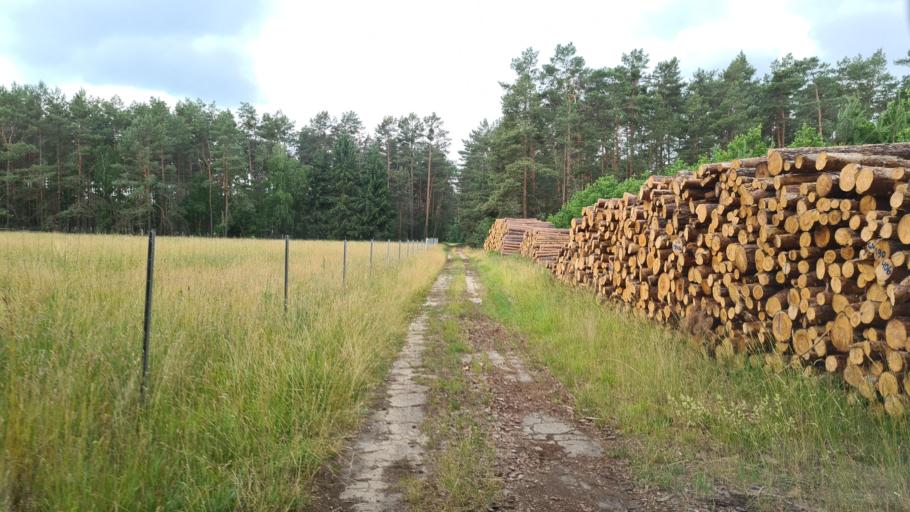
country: DE
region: Brandenburg
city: Crinitz
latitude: 51.7240
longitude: 13.7121
